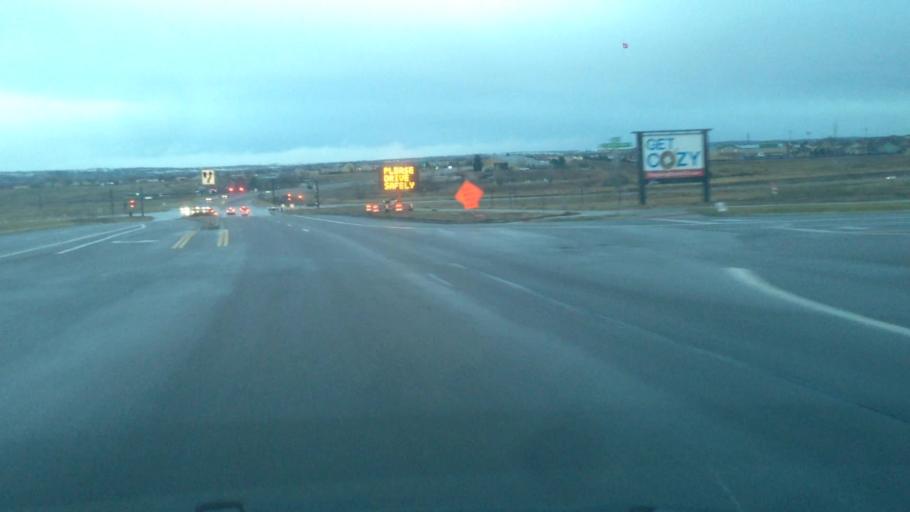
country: US
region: Colorado
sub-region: Douglas County
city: Stonegate
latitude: 39.5172
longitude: -104.8172
